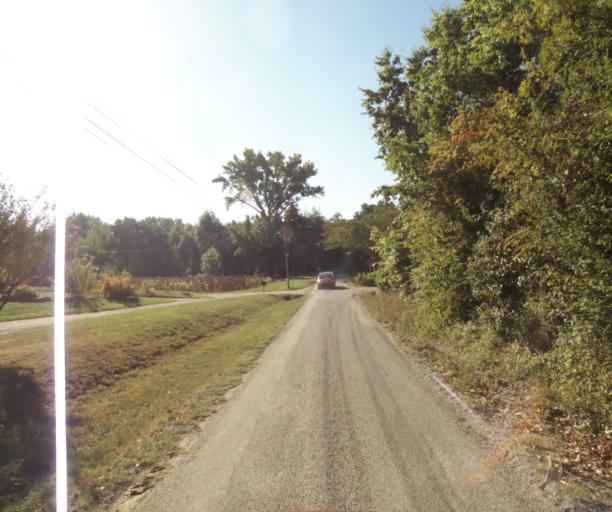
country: FR
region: Midi-Pyrenees
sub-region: Departement du Tarn-et-Garonne
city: Verdun-sur-Garonne
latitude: 43.8600
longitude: 1.2268
